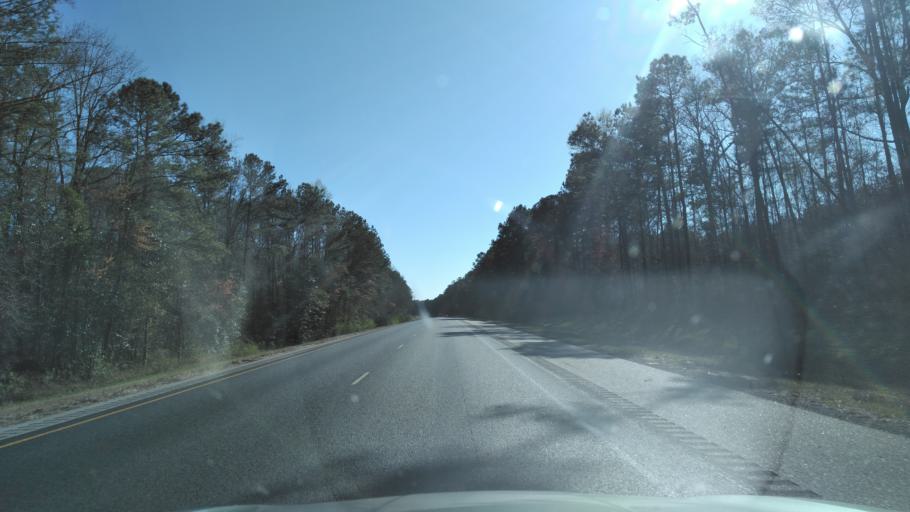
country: US
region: Alabama
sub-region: Butler County
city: Georgiana
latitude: 31.7110
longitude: -86.7343
